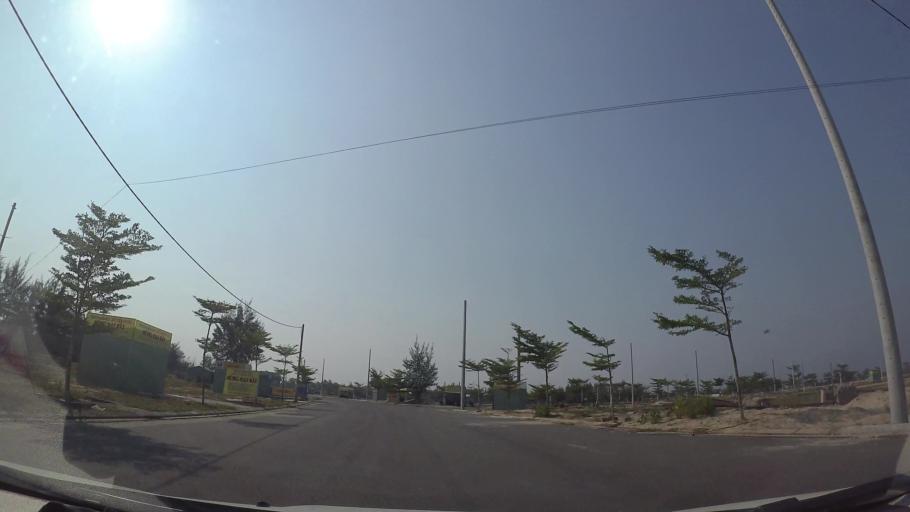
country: VN
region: Da Nang
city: Ngu Hanh Son
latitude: 15.9546
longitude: 108.2736
